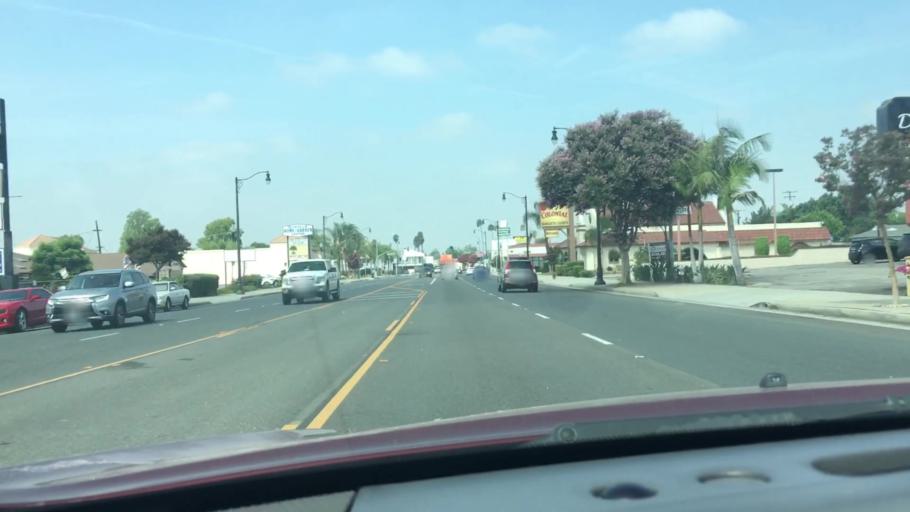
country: US
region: California
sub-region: Los Angeles County
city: East La Mirada
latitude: 33.9400
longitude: -117.9785
